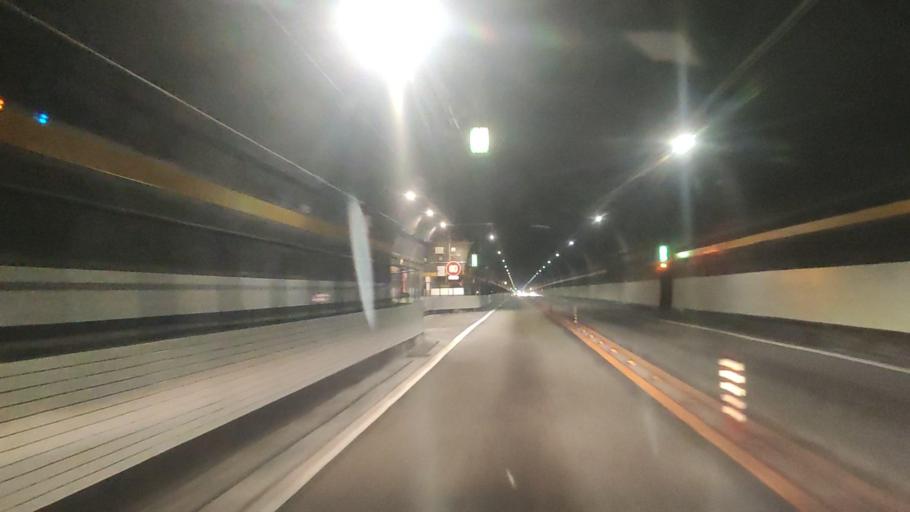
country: JP
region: Nagasaki
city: Obita
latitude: 32.7816
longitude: 129.8854
